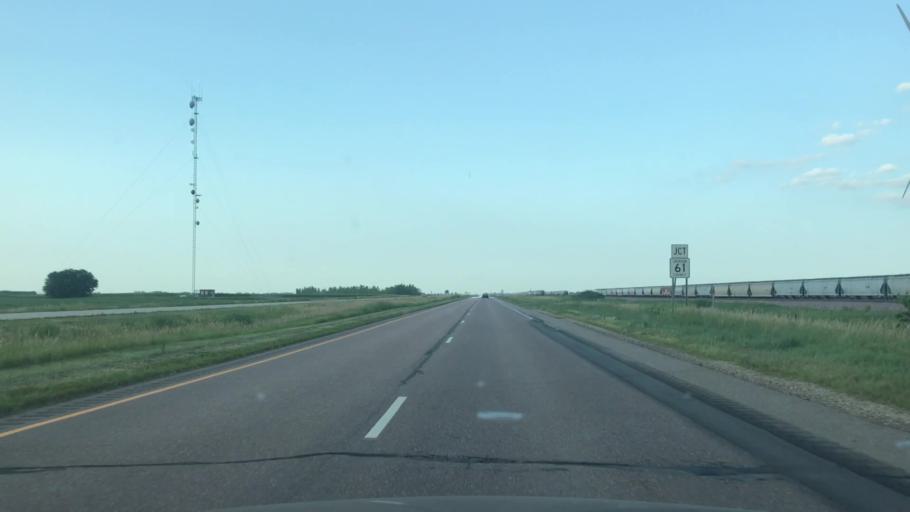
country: US
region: Minnesota
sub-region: Nobles County
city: Worthington
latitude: 43.7177
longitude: -95.4421
